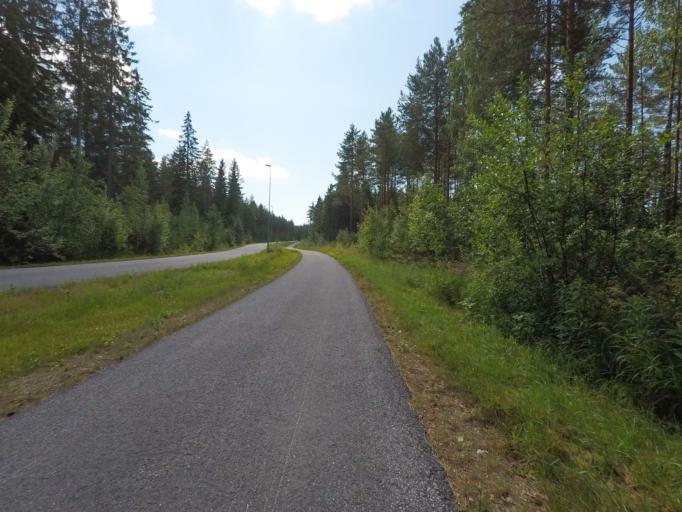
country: FI
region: Southern Savonia
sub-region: Mikkeli
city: Puumala
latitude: 61.5132
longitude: 28.1639
